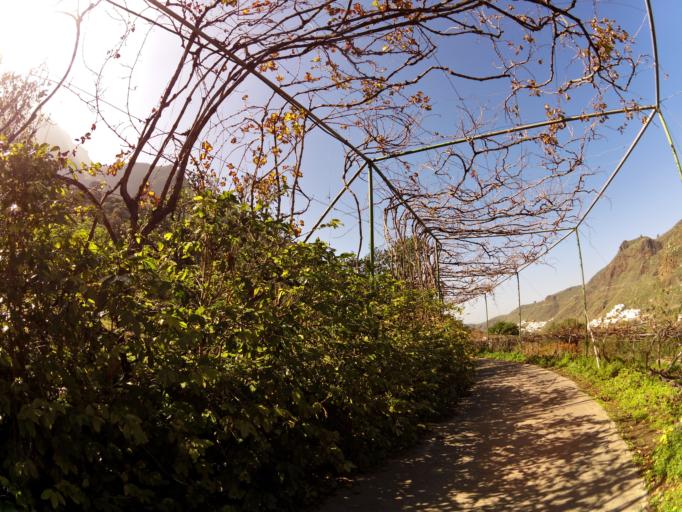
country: ES
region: Canary Islands
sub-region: Provincia de Las Palmas
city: Agaete
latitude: 28.0764
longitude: -15.6700
